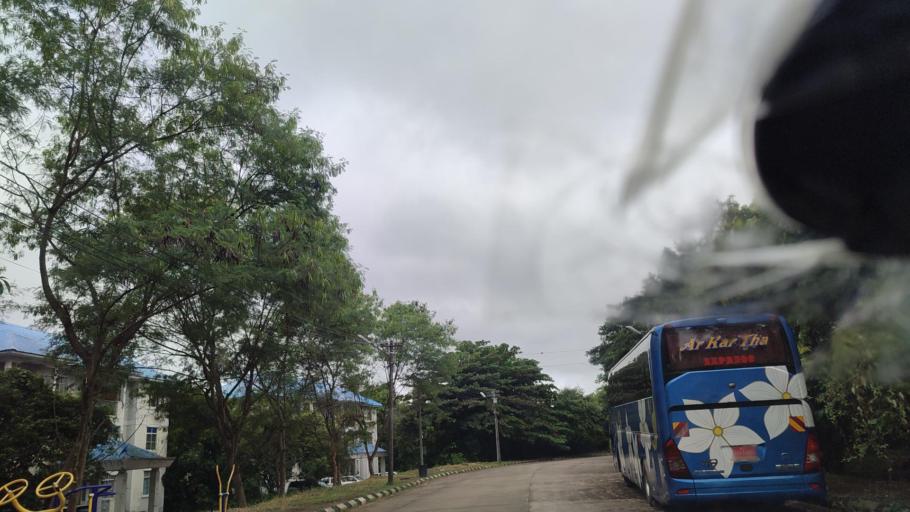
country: MM
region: Mandalay
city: Nay Pyi Taw
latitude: 19.7366
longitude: 96.0689
